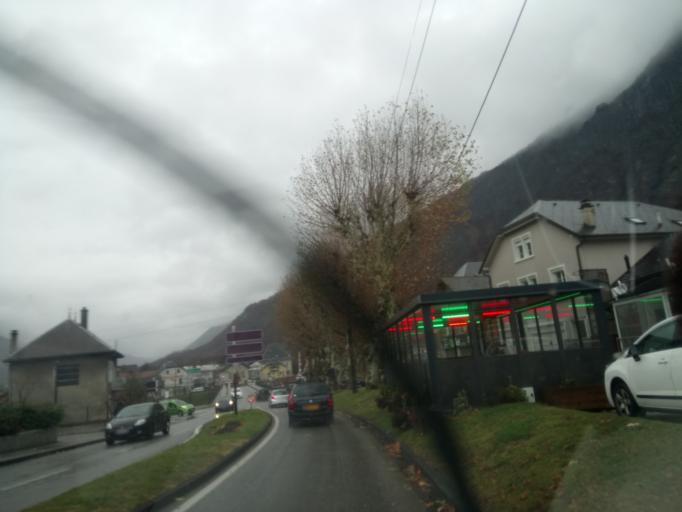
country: FR
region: Rhone-Alpes
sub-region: Departement de la Savoie
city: Saint-Jean-de-Maurienne
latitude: 45.2721
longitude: 6.3508
